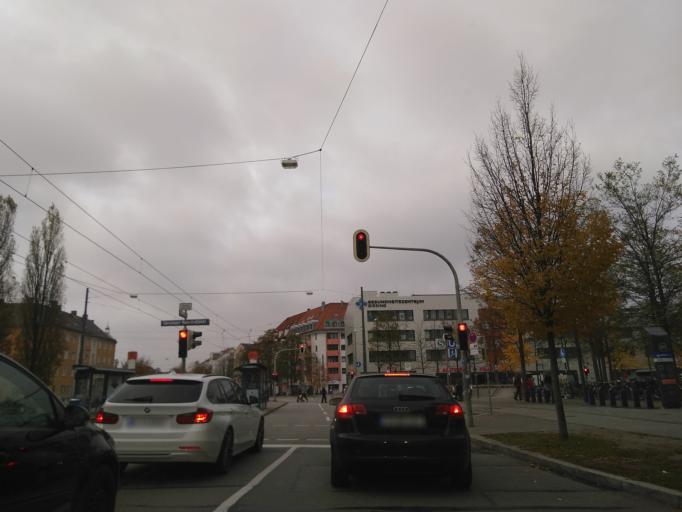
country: DE
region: Bavaria
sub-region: Upper Bavaria
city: Munich
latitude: 48.1102
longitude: 11.5950
